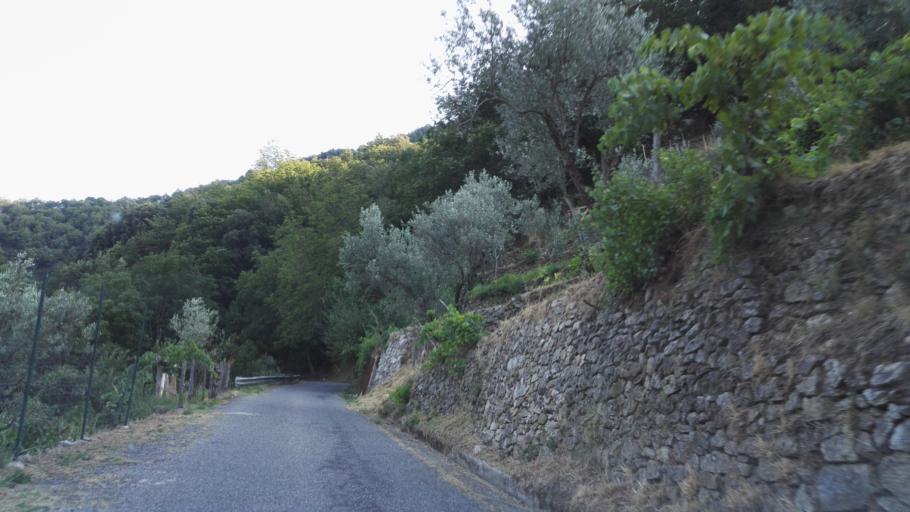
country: IT
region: Calabria
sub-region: Provincia di Vibo-Valentia
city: Nardodipace
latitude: 38.4461
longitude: 16.3406
